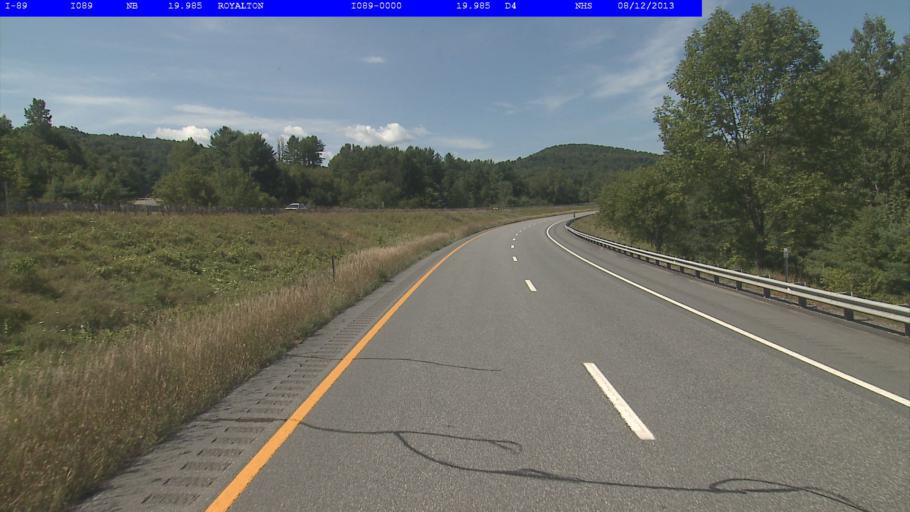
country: US
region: Vermont
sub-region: Orange County
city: Randolph
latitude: 43.8120
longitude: -72.5450
